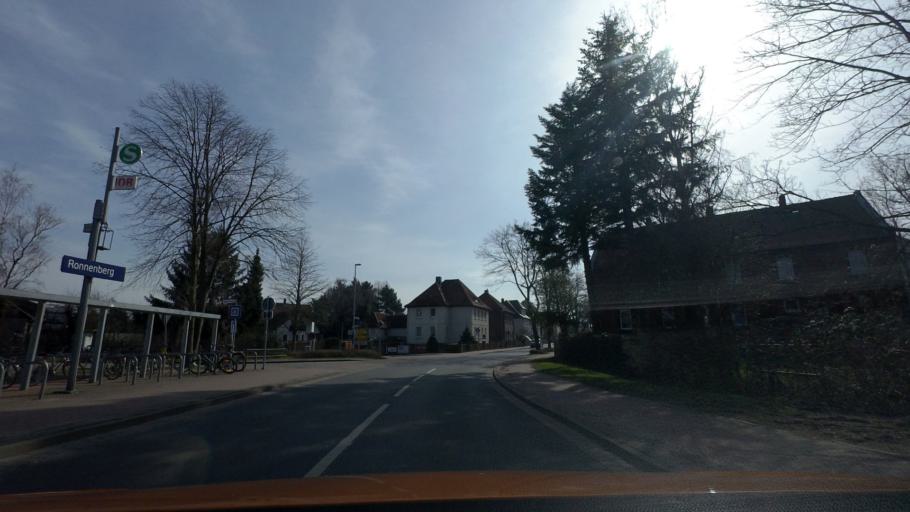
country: DE
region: Lower Saxony
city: Ronnenberg
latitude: 52.3221
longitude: 9.6510
